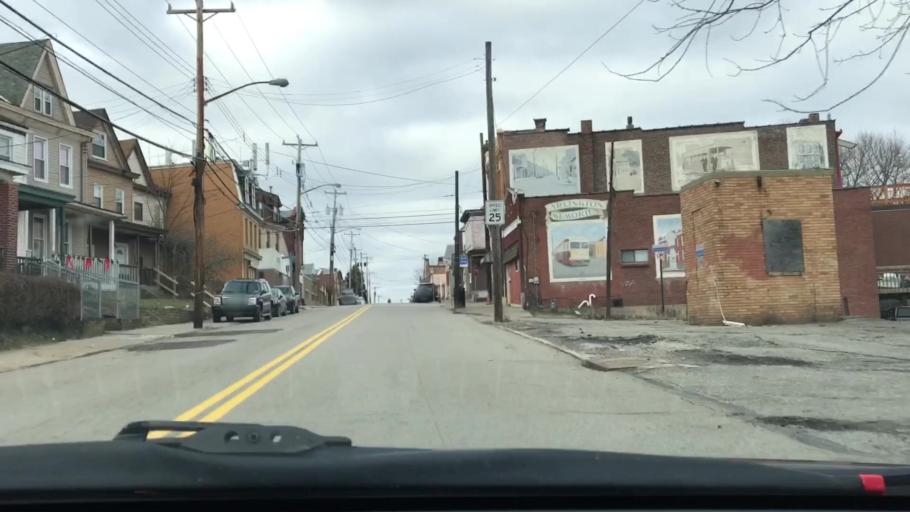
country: US
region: Pennsylvania
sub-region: Allegheny County
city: Mount Oliver
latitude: 40.4175
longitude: -79.9722
